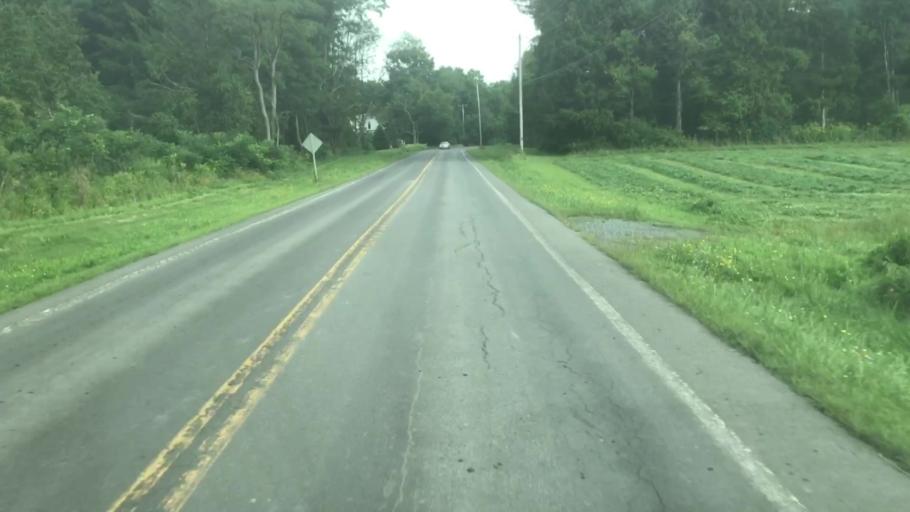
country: US
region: New York
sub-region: Onondaga County
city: Skaneateles
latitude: 42.8664
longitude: -76.4486
